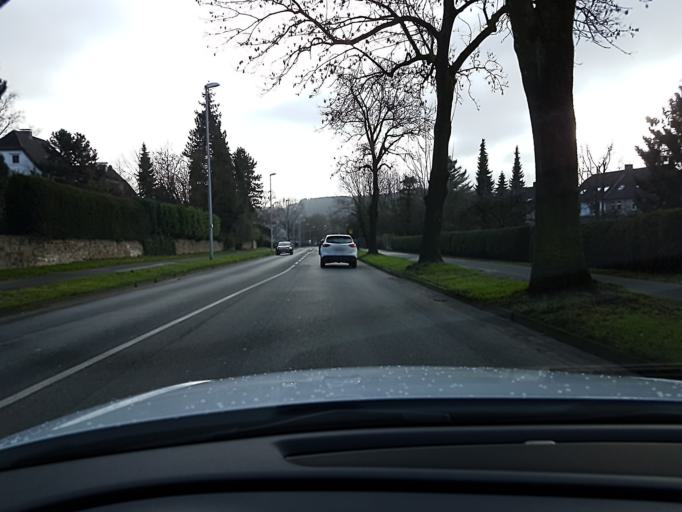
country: DE
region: North Rhine-Westphalia
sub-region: Regierungsbezirk Dusseldorf
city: Heiligenhaus
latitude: 51.3667
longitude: 6.9424
